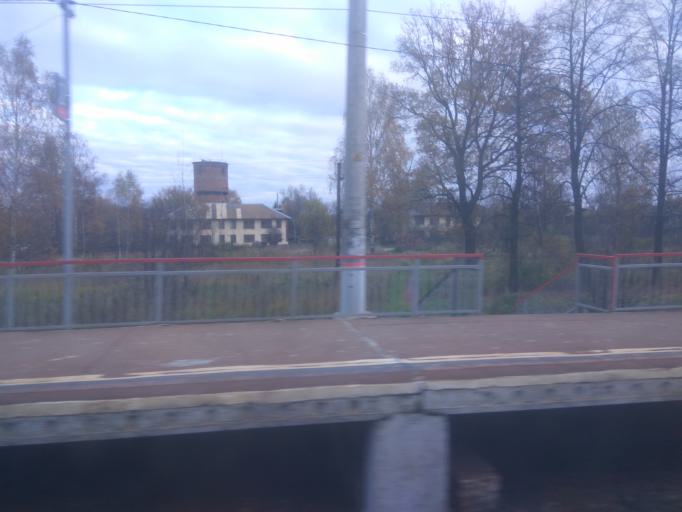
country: RU
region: Moskovskaya
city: Aprelevka
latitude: 55.5669
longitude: 37.0933
